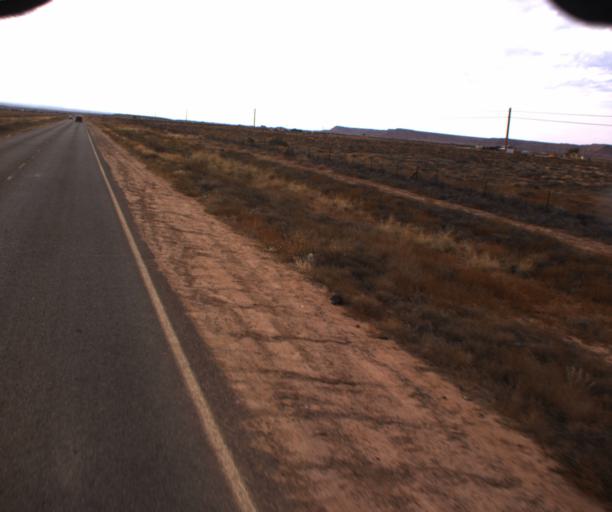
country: US
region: Arizona
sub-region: Apache County
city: Many Farms
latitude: 36.3285
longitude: -109.6207
